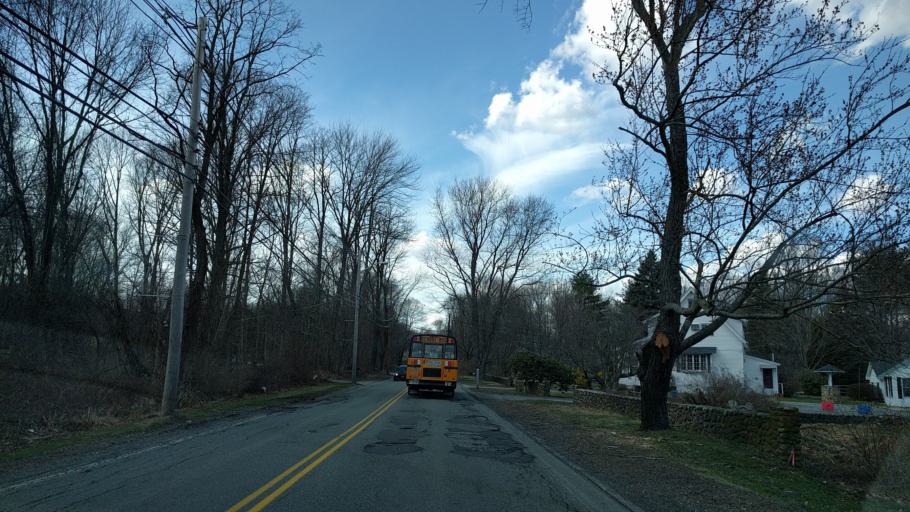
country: US
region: Massachusetts
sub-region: Worcester County
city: Mendon
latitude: 42.1026
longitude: -71.5450
